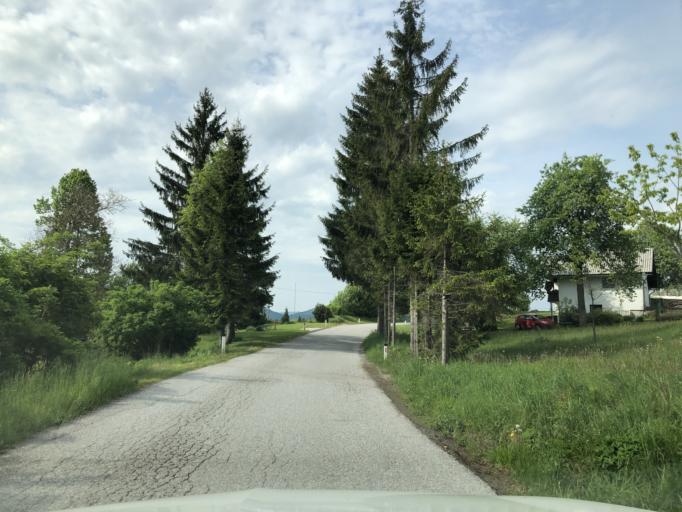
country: SI
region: Bloke
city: Nova Vas
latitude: 45.7981
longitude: 14.5450
